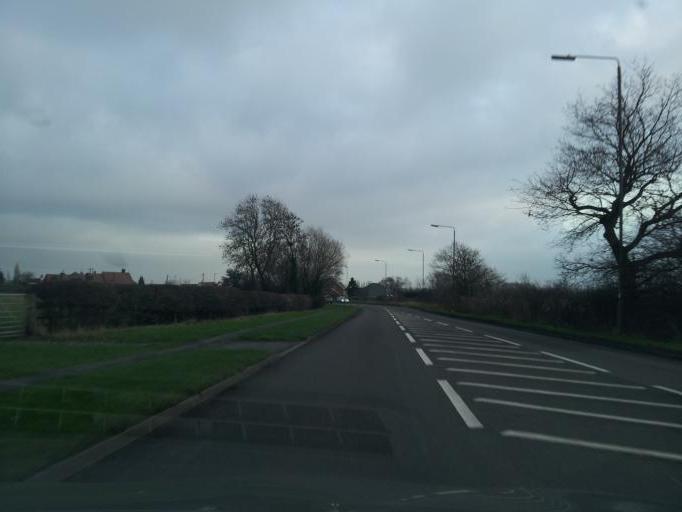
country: GB
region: England
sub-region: Derbyshire
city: Repton
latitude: 52.8528
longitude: -1.5773
